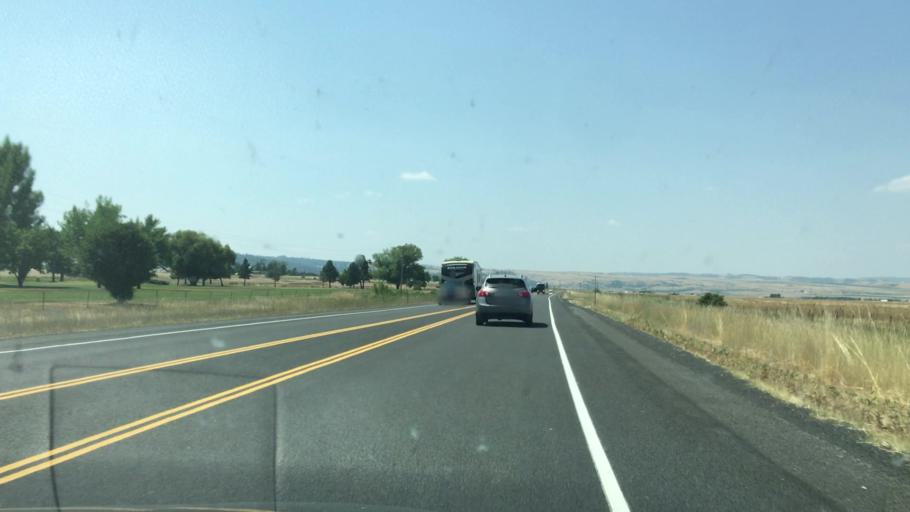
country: US
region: Idaho
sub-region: Idaho County
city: Grangeville
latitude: 45.9129
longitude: -116.1614
